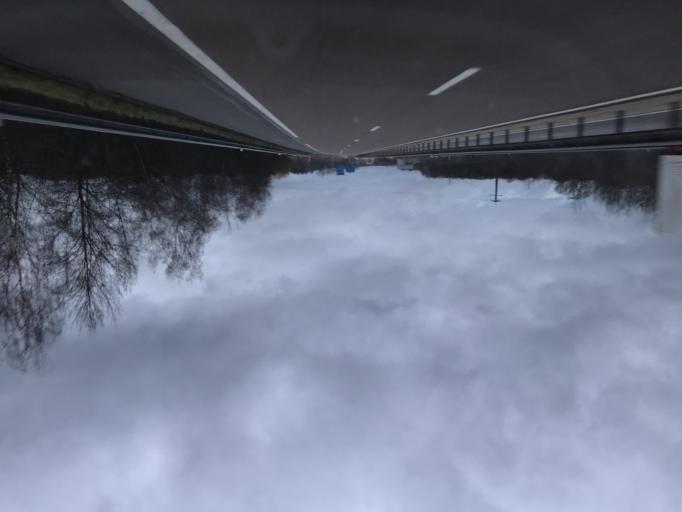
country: FR
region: Franche-Comte
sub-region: Departement du Jura
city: Damparis
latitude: 47.1113
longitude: 5.3970
